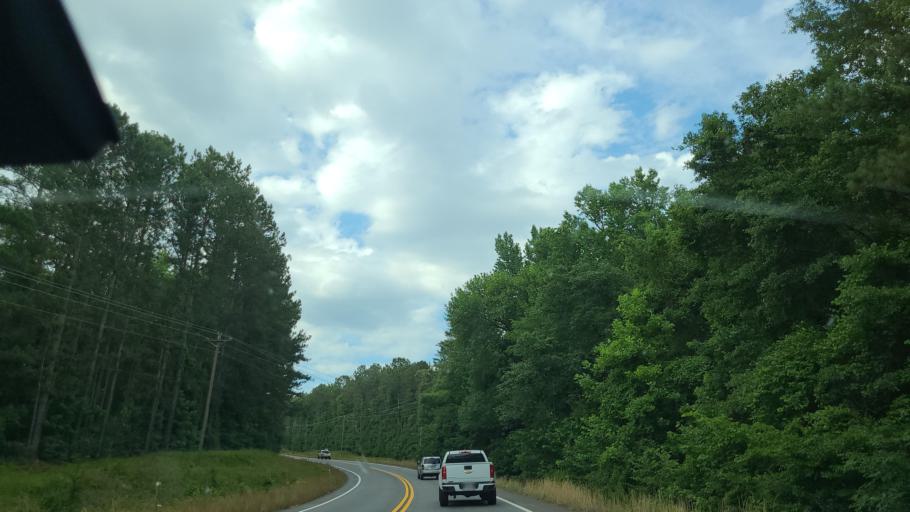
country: US
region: Georgia
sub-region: Putnam County
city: Eatonton
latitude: 33.1892
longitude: -83.4342
